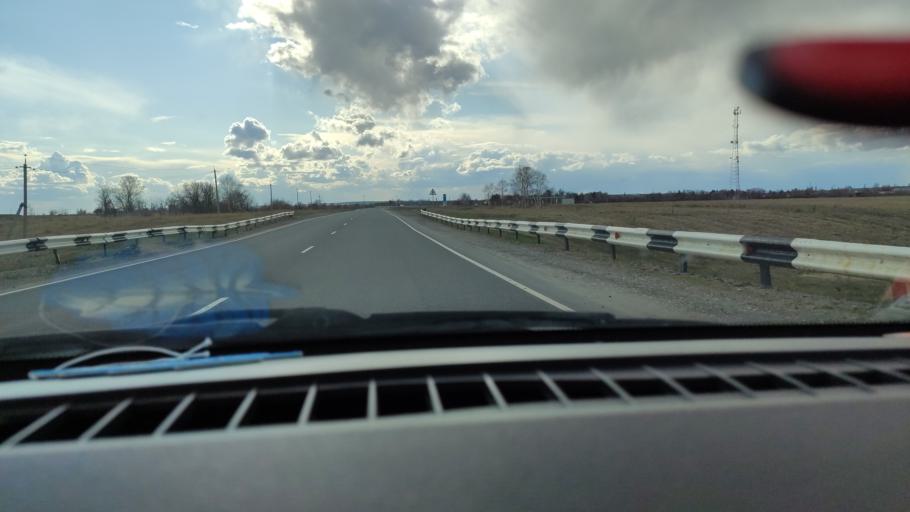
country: RU
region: Saratov
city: Sennoy
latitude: 52.1507
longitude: 46.9757
